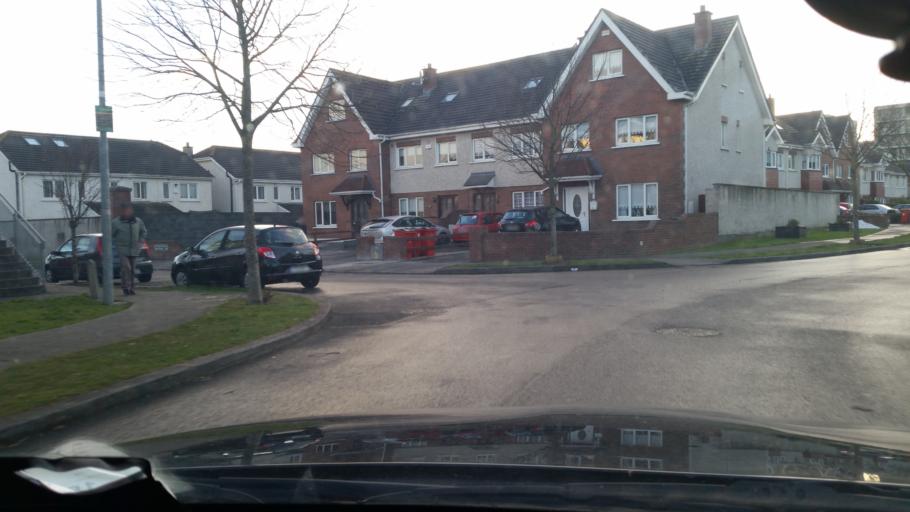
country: IE
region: Leinster
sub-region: Dublin City
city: Finglas
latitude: 53.4039
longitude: -6.2994
